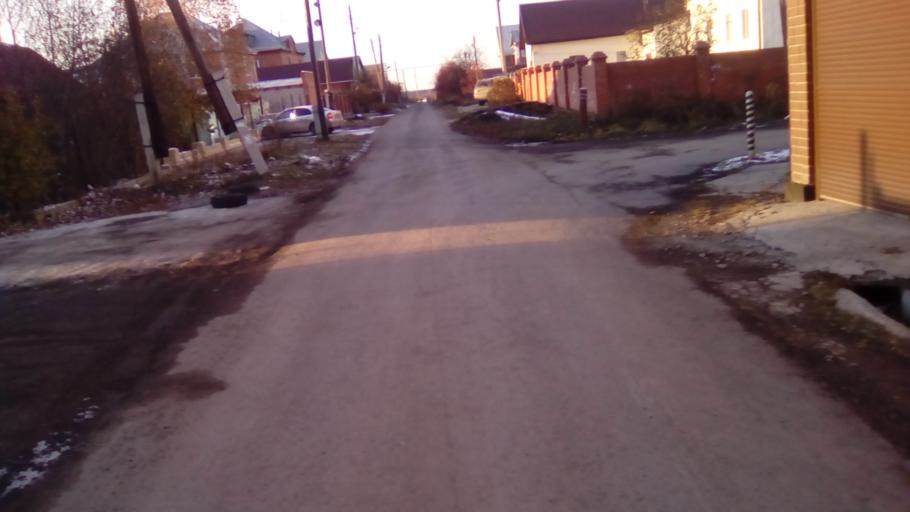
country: RU
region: Tjumen
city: Moskovskiy
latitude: 57.2213
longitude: 65.3644
